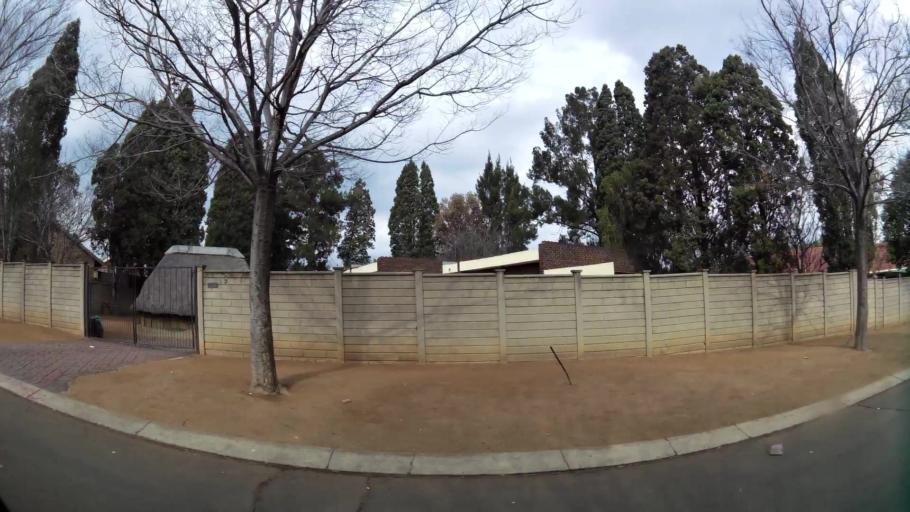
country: ZA
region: Gauteng
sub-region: Sedibeng District Municipality
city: Vanderbijlpark
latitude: -26.7052
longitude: 27.8033
